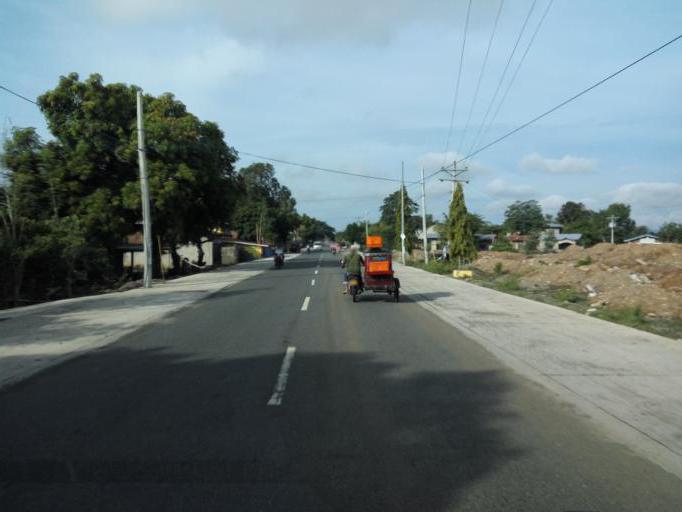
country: PH
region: Cagayan Valley
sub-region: Province of Isabela
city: Cabagan
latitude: 17.4372
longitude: 121.7776
